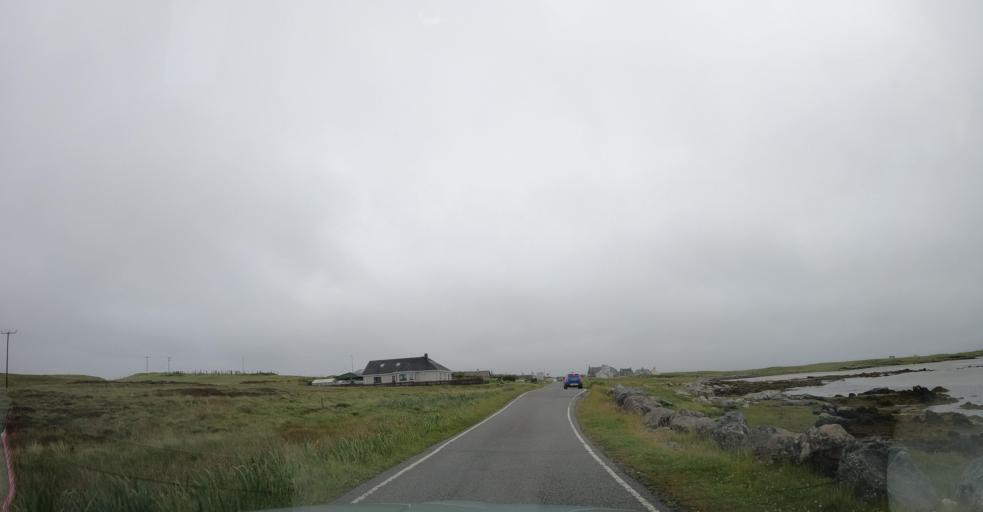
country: GB
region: Scotland
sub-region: Eilean Siar
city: Isle of North Uist
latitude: 57.5549
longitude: -7.3370
